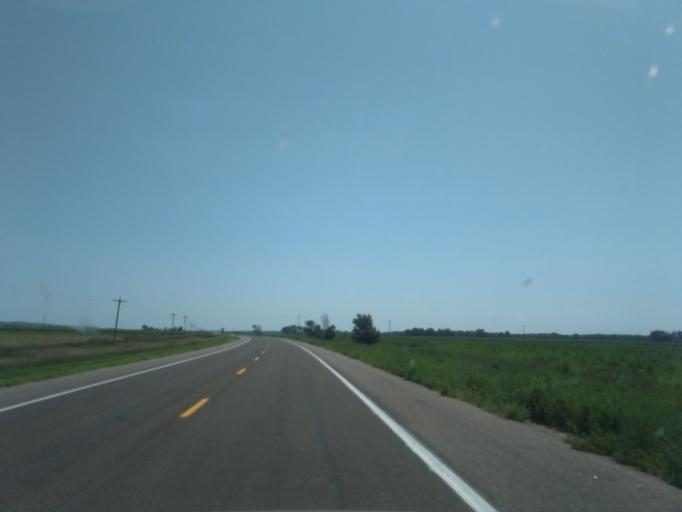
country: US
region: Nebraska
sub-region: Dundy County
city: Benkelman
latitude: 40.1257
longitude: -101.3195
